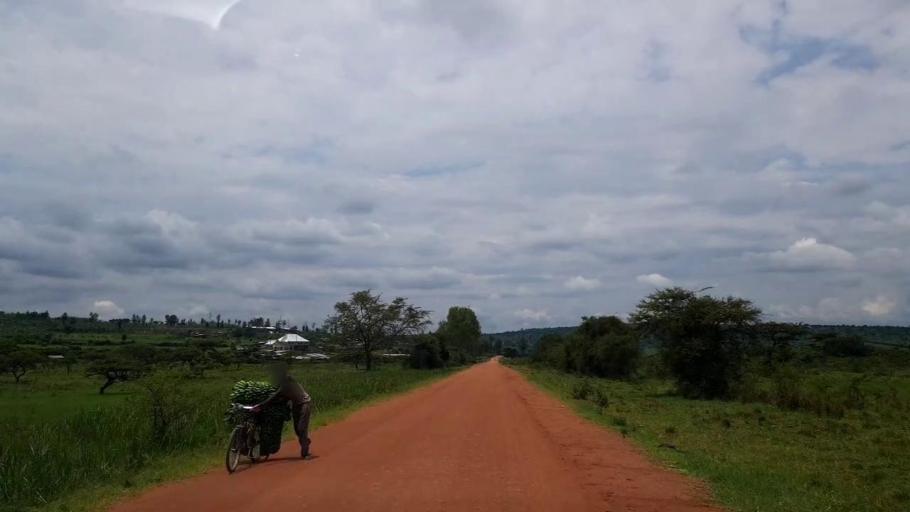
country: RW
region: Northern Province
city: Byumba
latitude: -1.5447
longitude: 30.3602
